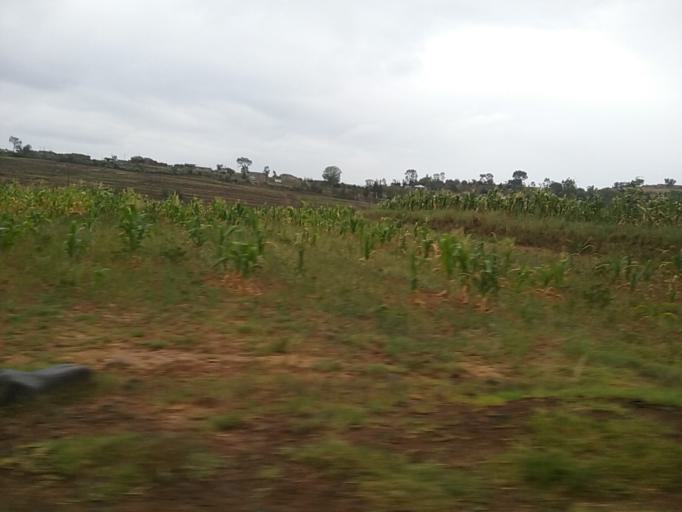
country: LS
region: Berea
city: Teyateyaneng
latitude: -29.1306
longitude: 27.7389
